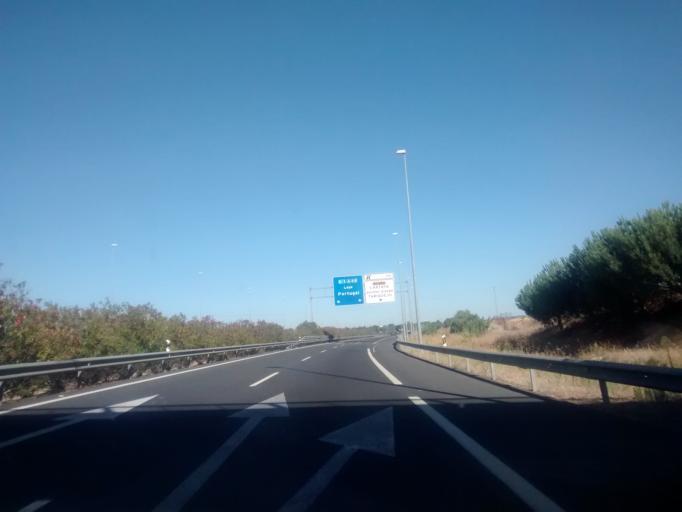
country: ES
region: Andalusia
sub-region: Provincia de Huelva
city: Cartaya
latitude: 37.3309
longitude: -7.1461
